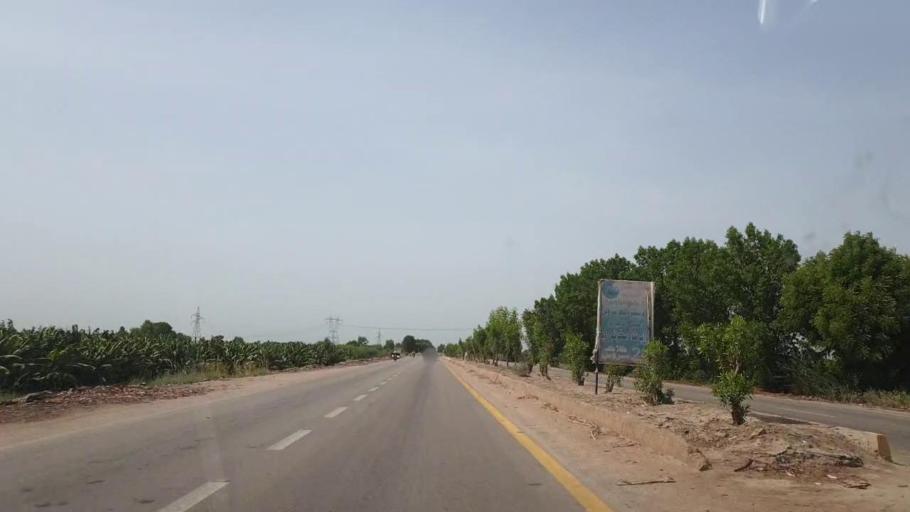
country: PK
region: Sindh
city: Sakrand
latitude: 26.1853
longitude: 68.2910
